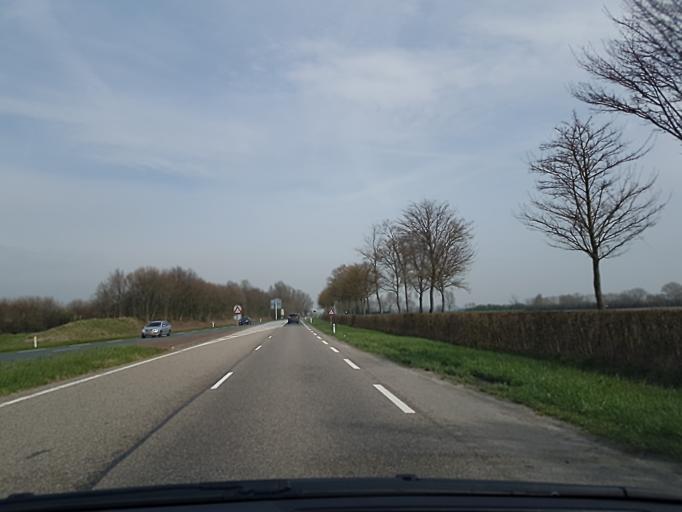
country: NL
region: Zeeland
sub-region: Gemeente Terneuzen
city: Sluiskil
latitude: 51.3081
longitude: 3.8638
